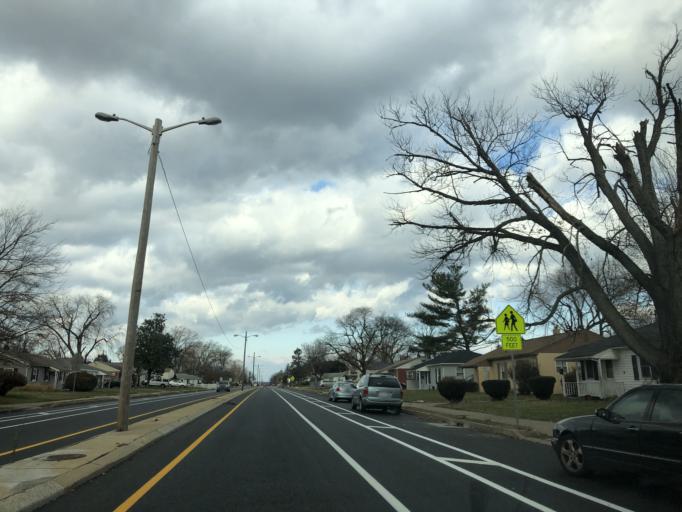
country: US
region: Delaware
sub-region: New Castle County
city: Wilmington Manor
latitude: 39.7029
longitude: -75.5570
